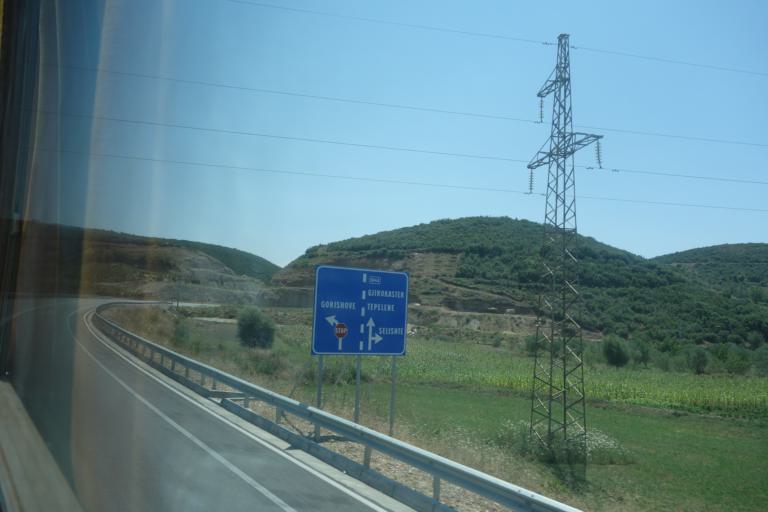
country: AL
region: Vlore
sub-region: Rrethi i Vlores
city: Selenice
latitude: 40.5662
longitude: 19.6465
